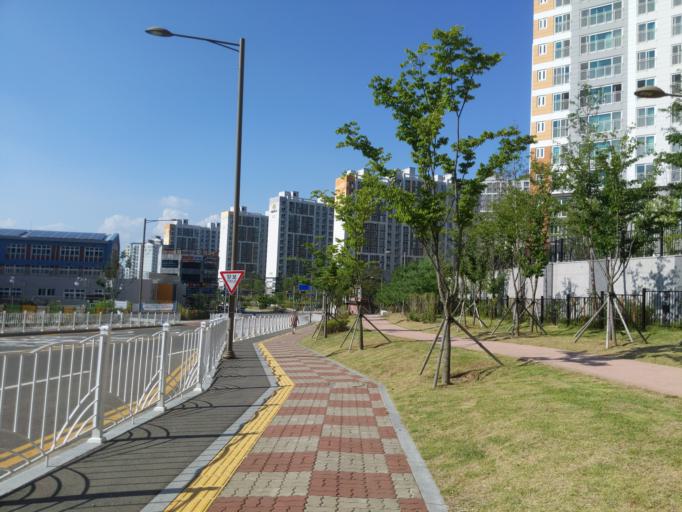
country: KR
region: Daegu
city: Hwawon
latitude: 35.7982
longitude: 128.5295
